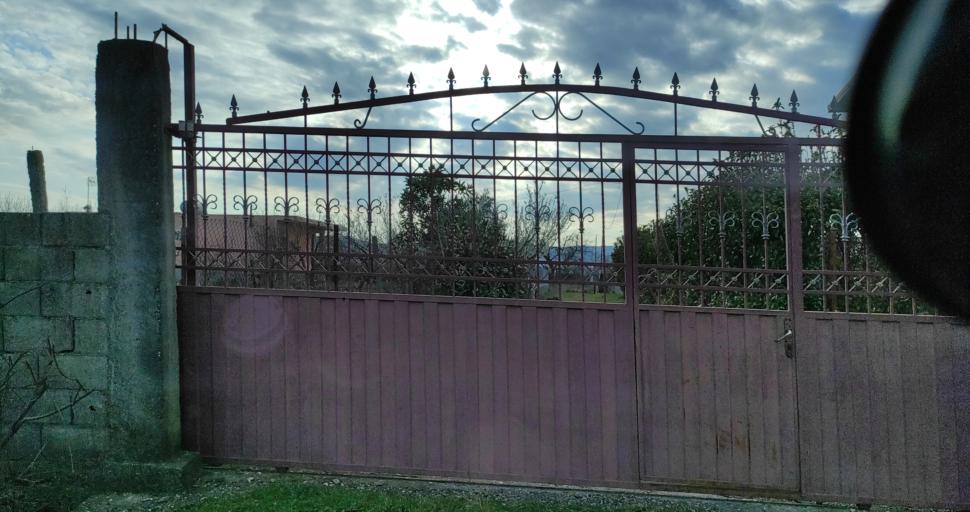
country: AL
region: Lezhe
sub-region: Rrethi i Lezhes
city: Kallmeti i Madh
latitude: 41.8804
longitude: 19.6646
